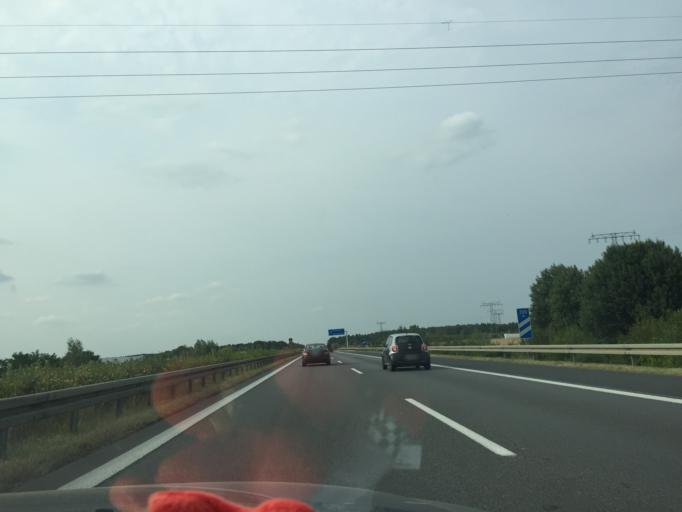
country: DE
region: Brandenburg
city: Mittenwalde
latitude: 52.2597
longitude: 13.5806
